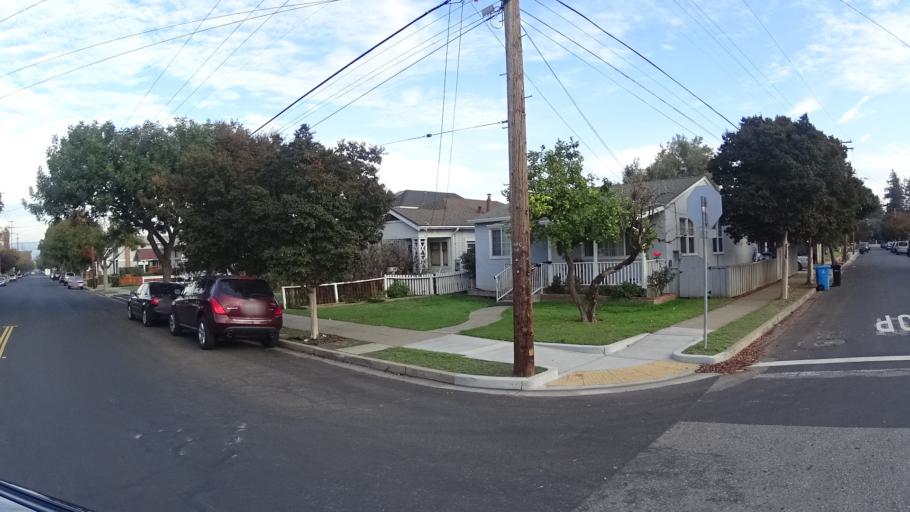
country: US
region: California
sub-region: Santa Clara County
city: Santa Clara
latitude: 37.3493
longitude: -121.9555
